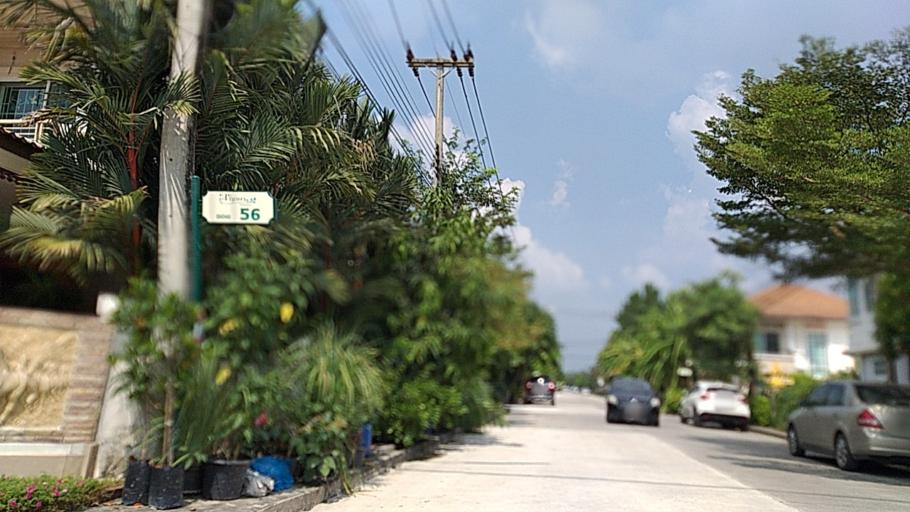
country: TH
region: Pathum Thani
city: Ban Rangsit
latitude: 14.0436
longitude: 100.7652
